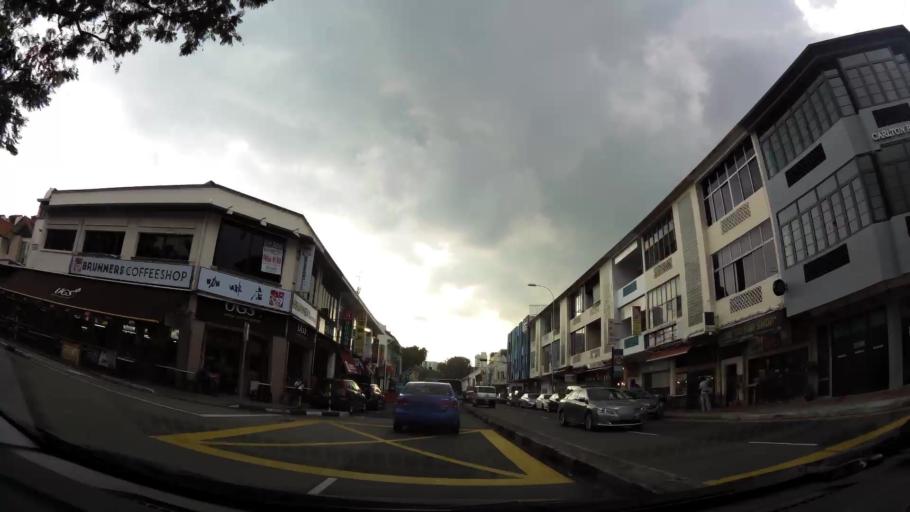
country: SG
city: Singapore
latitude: 1.3077
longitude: 103.9076
